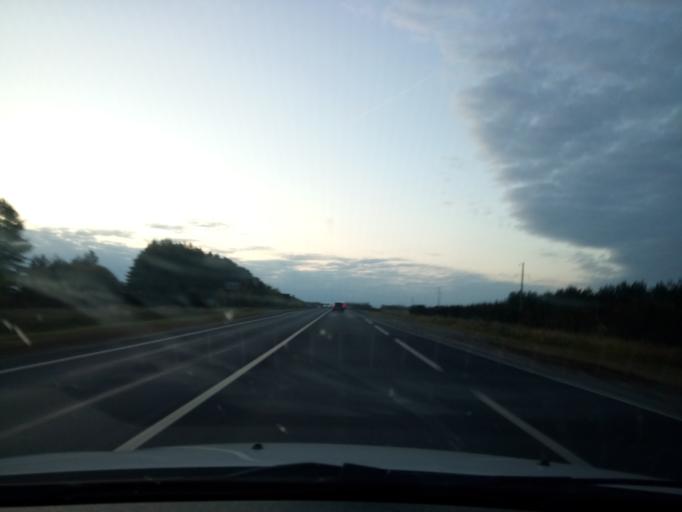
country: RU
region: Nizjnij Novgorod
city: Bol'shoye Murashkino
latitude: 55.8945
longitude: 44.7340
